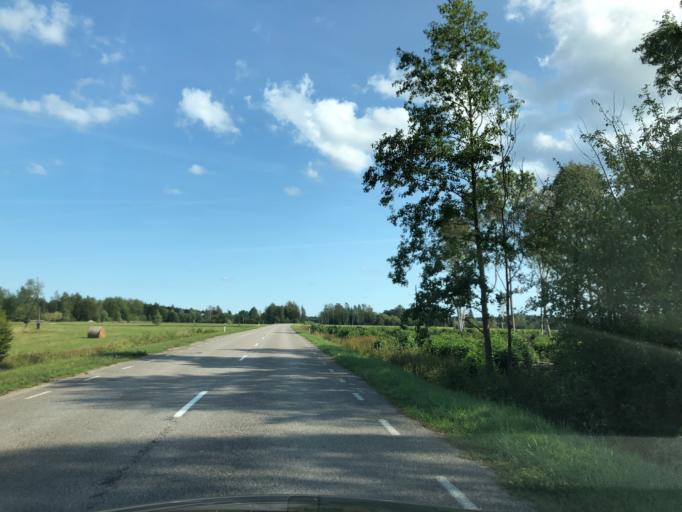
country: EE
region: Hiiumaa
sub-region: Kaerdla linn
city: Kardla
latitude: 58.7175
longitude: 22.5684
